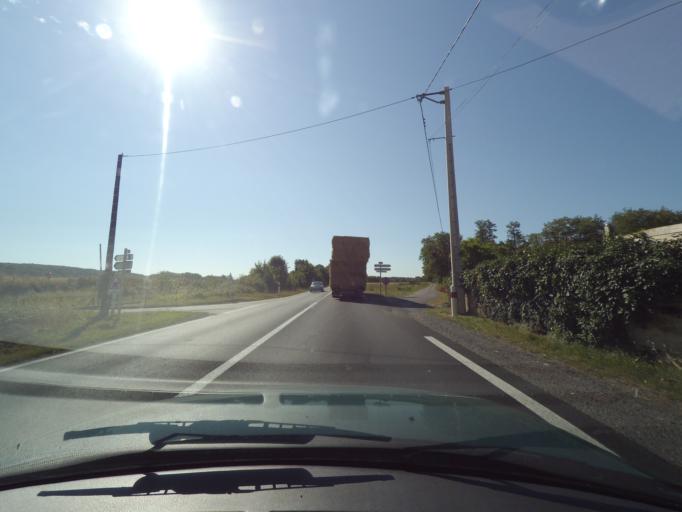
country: FR
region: Poitou-Charentes
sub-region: Departement de la Vienne
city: Lussac-les-Chateaux
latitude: 46.4171
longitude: 0.6812
